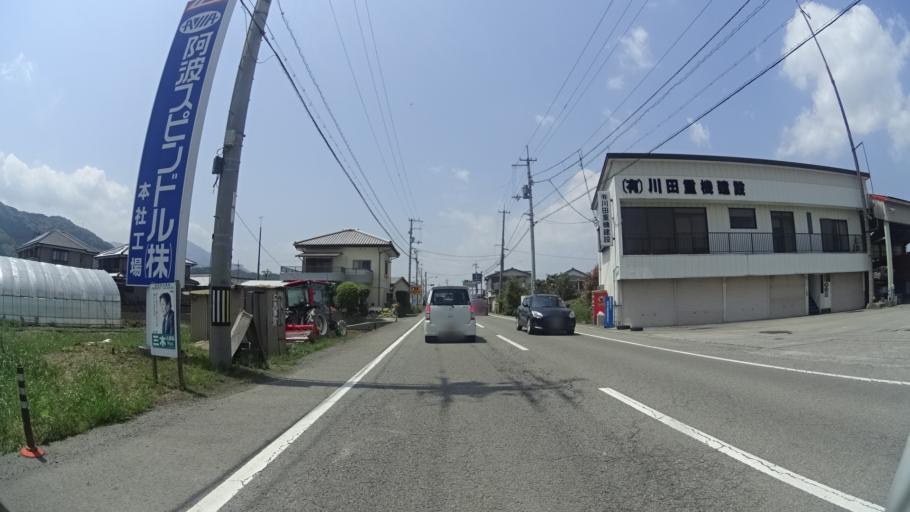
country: JP
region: Tokushima
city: Kamojimacho-jogejima
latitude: 34.0636
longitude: 134.2690
